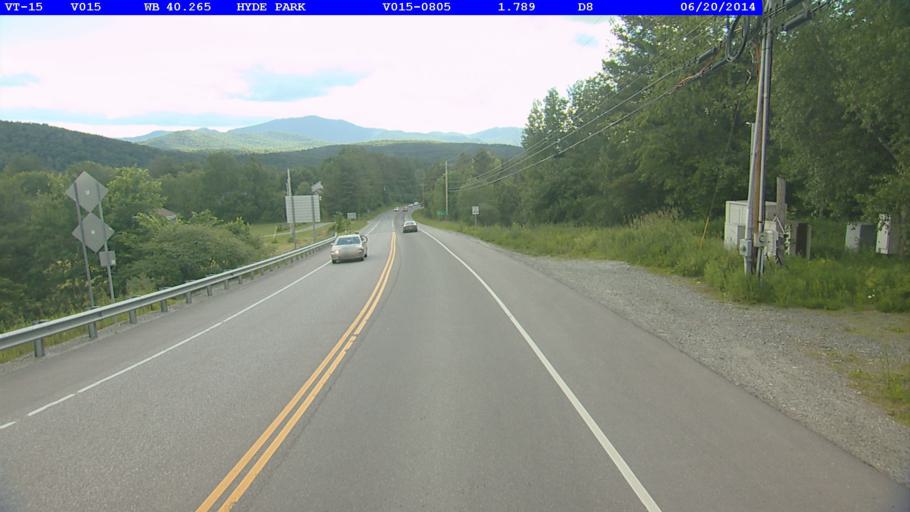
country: US
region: Vermont
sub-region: Lamoille County
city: Hyde Park
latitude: 44.5974
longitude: -72.6168
